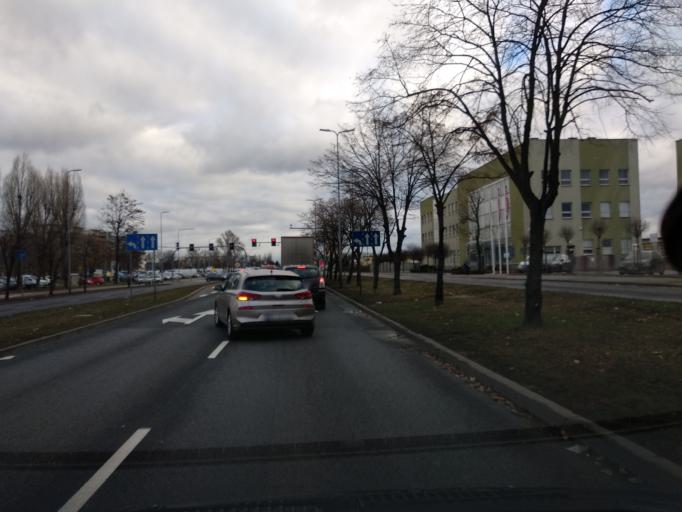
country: PL
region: Greater Poland Voivodeship
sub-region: Kalisz
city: Kalisz
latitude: 51.7460
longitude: 18.0588
